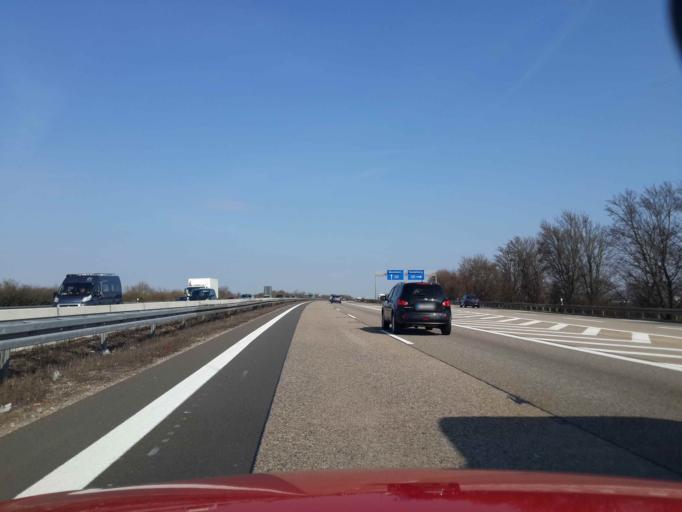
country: DE
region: Baden-Wuerttemberg
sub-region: Karlsruhe Region
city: Eppelheim
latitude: 49.4122
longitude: 8.6347
